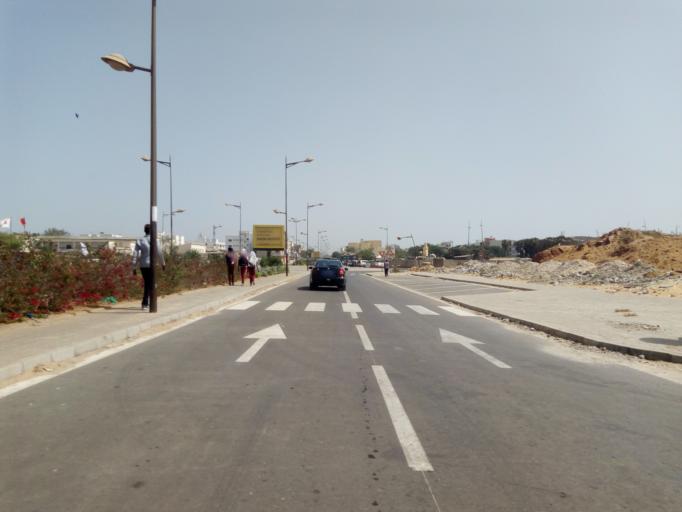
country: SN
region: Dakar
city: Dakar
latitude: 14.7008
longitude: -17.4505
